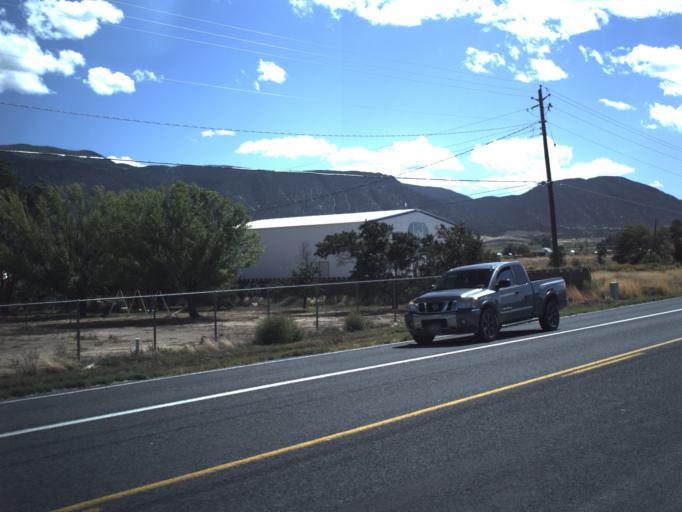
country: US
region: Utah
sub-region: Iron County
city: Enoch
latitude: 37.7552
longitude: -113.0553
